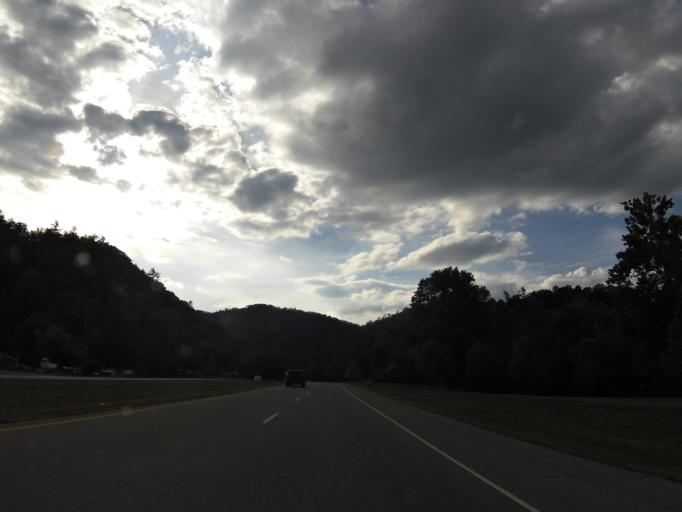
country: US
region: Tennessee
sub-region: Blount County
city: Wildwood
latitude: 35.6823
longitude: -83.7888
